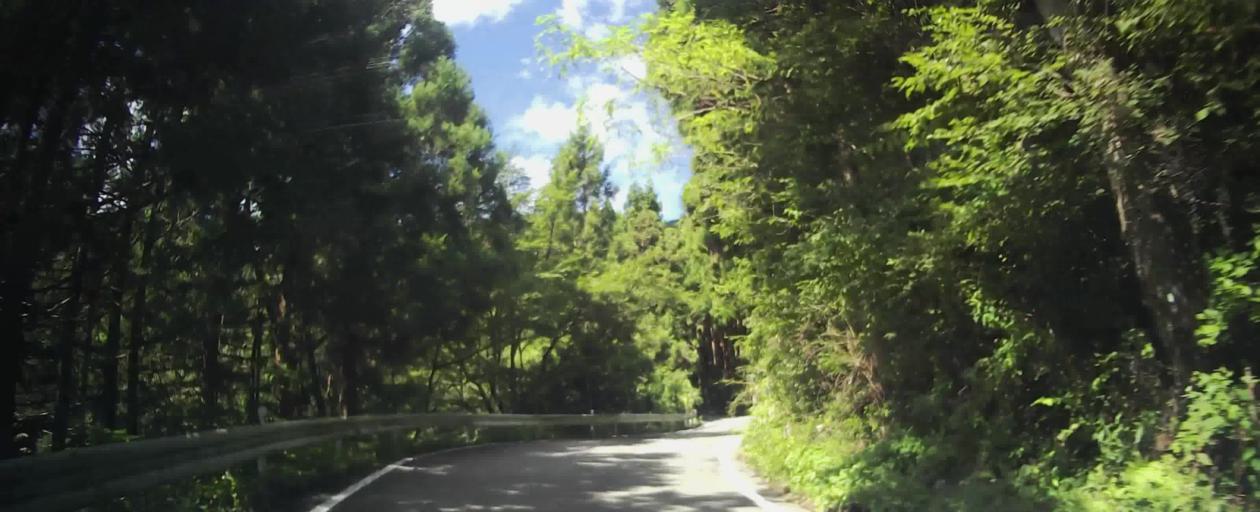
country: JP
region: Gunma
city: Shibukawa
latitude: 36.4555
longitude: 138.8976
